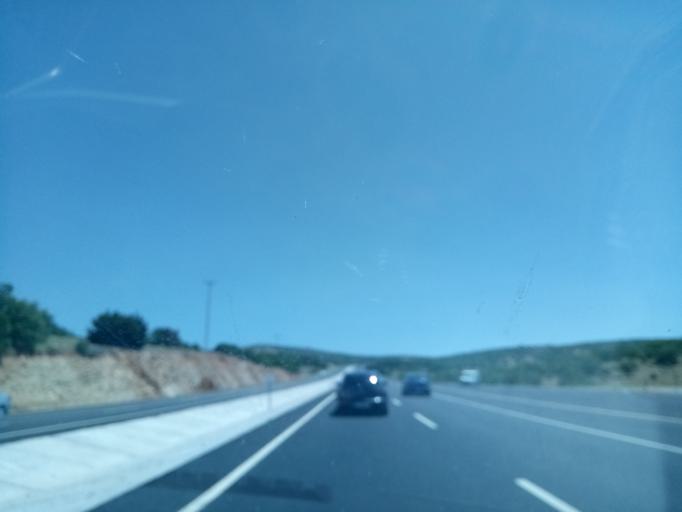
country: TR
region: Konya
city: Kiziloren
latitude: 37.7651
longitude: 32.2449
